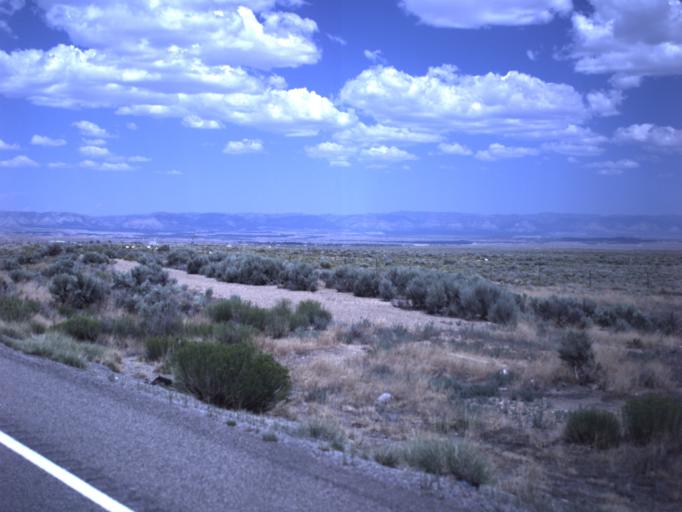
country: US
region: Utah
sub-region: Carbon County
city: Price
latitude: 39.4791
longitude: -110.8531
